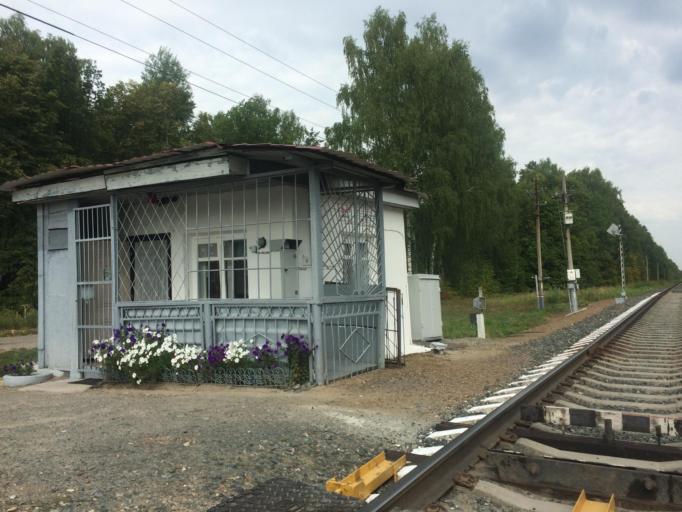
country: RU
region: Mariy-El
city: Yoshkar-Ola
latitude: 56.5607
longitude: 47.9804
